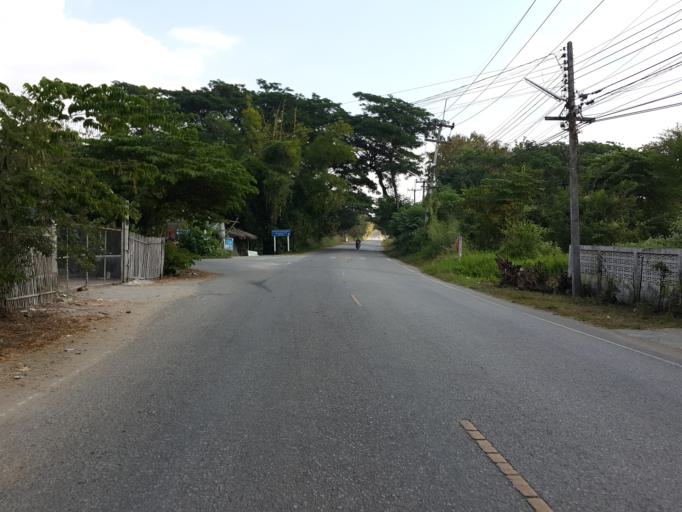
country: TH
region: Chiang Mai
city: San Kamphaeng
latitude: 18.7282
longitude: 99.1360
